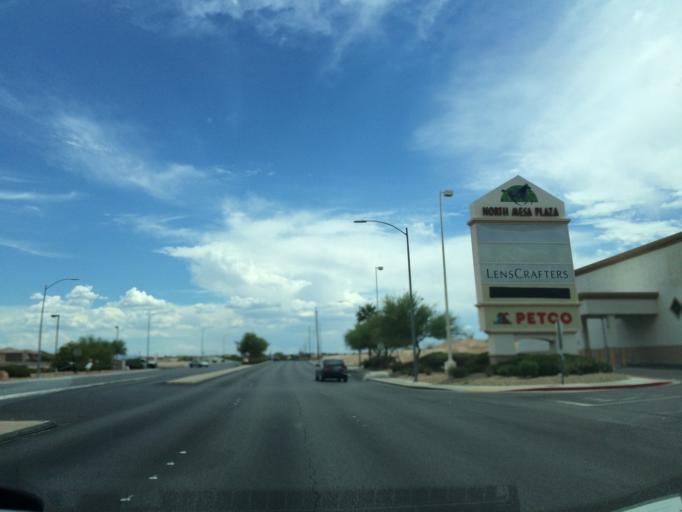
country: US
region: Nevada
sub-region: Clark County
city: North Las Vegas
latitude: 36.2383
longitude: -115.1621
